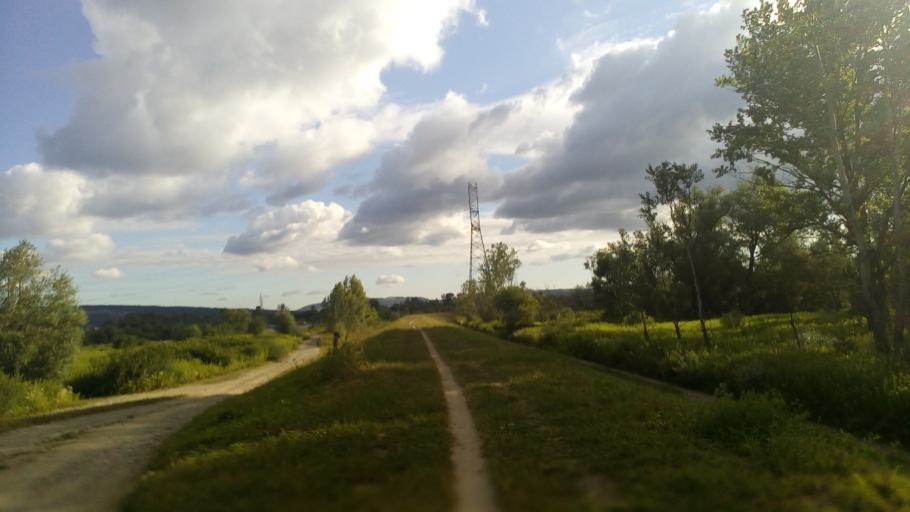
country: PL
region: Lesser Poland Voivodeship
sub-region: Powiat nowosadecki
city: Stary Sacz
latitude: 49.5927
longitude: 20.6548
